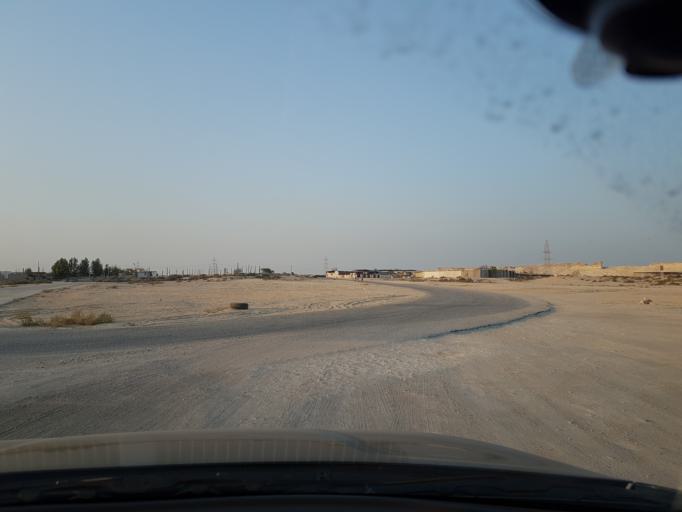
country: BH
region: Central Governorate
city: Dar Kulayb
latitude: 25.9991
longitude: 50.5847
